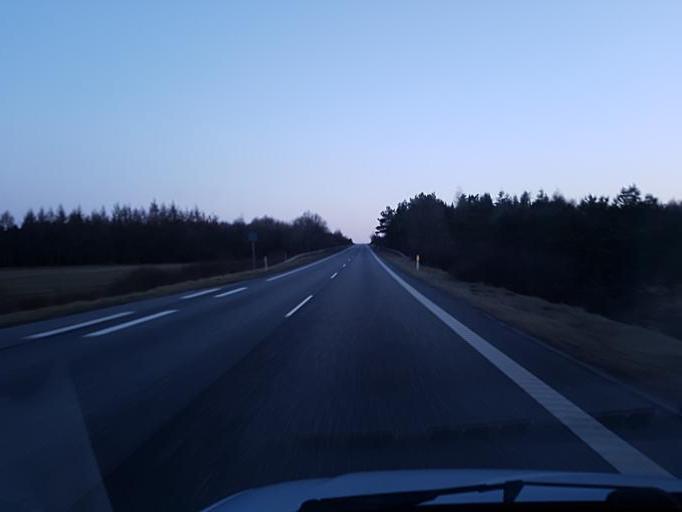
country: DK
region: Central Jutland
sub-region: Holstebro Kommune
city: Holstebro
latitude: 56.2316
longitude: 8.6029
